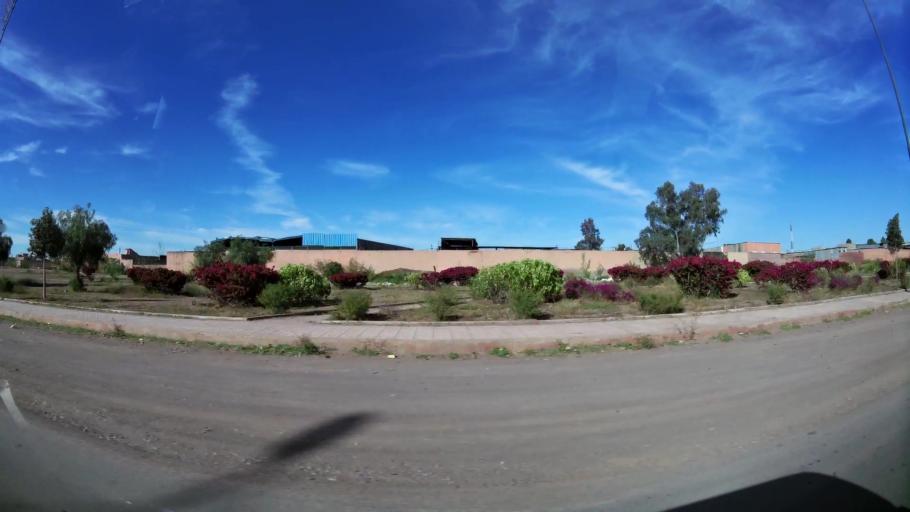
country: MA
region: Marrakech-Tensift-Al Haouz
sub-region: Marrakech
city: Marrakesh
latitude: 31.6817
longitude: -8.0562
